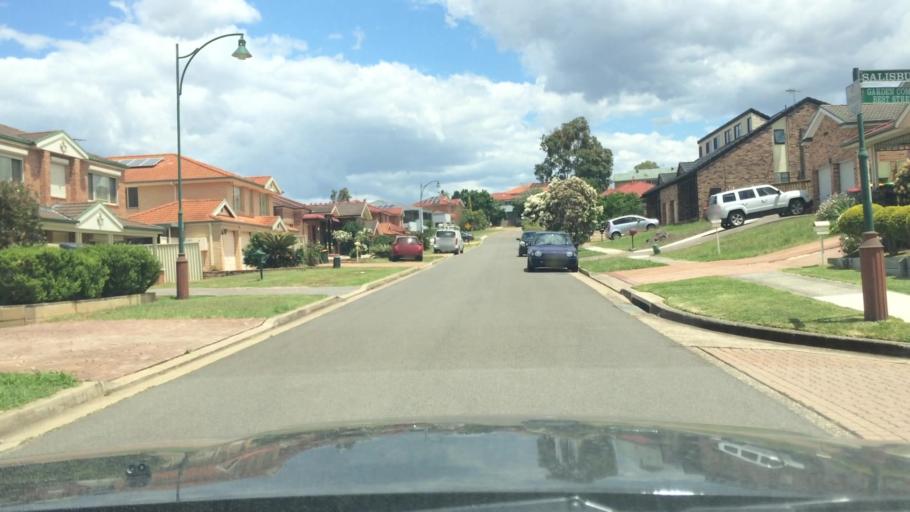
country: AU
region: New South Wales
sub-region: Campbelltown Municipality
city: Denham Court
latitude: -33.9398
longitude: 150.8351
